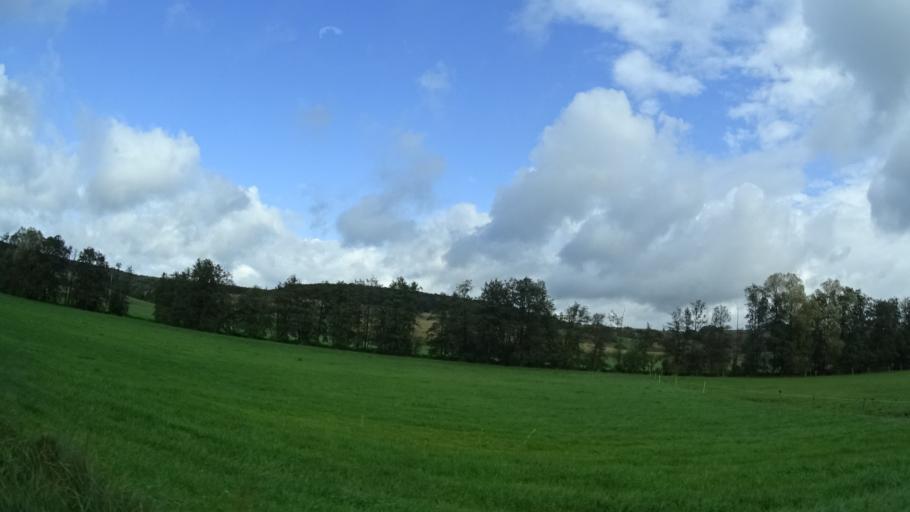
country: DE
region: Bavaria
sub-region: Upper Franconia
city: Burgwindheim
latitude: 49.8770
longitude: 10.6097
